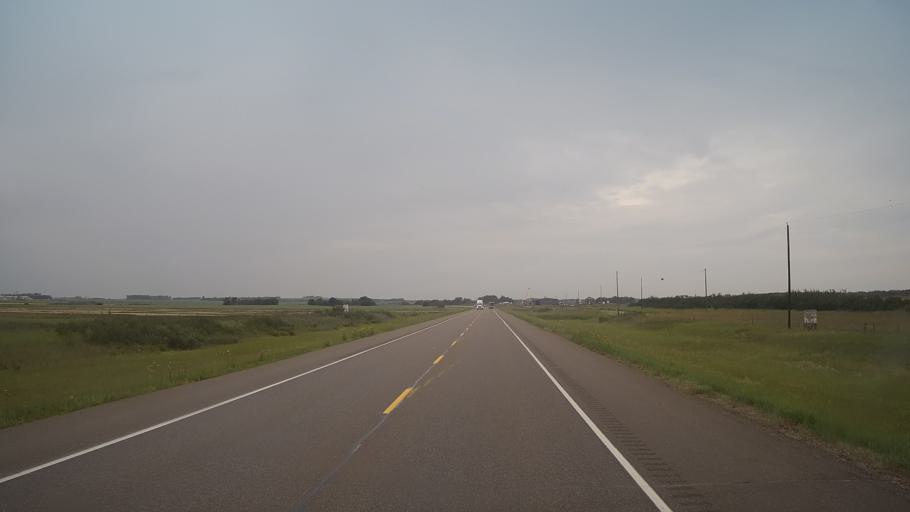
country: CA
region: Saskatchewan
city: Dalmeny
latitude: 52.1292
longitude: -106.8878
